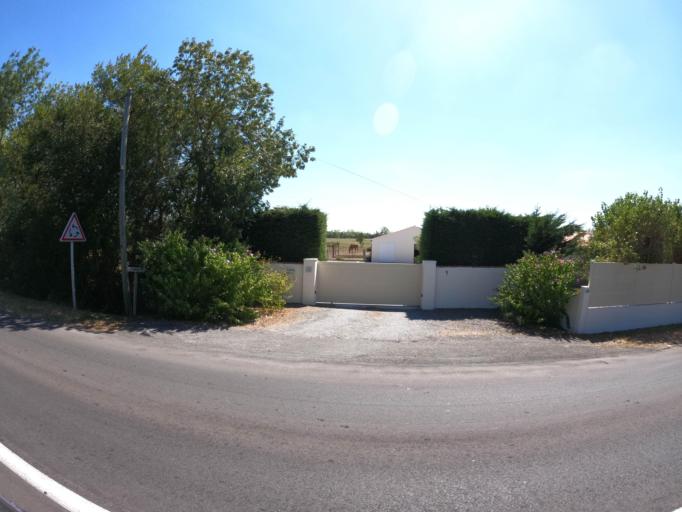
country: FR
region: Pays de la Loire
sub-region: Departement de la Vendee
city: Sallertaine
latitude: 46.8279
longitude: -1.9460
